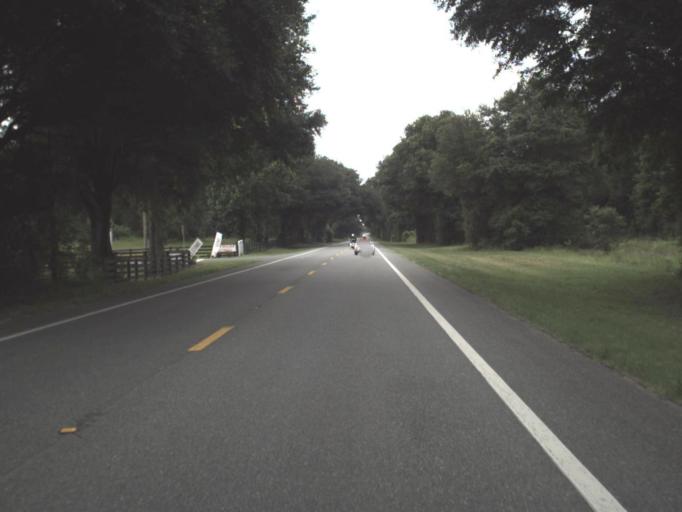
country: US
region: Florida
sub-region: Alachua County
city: Newberry
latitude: 29.5983
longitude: -82.5716
